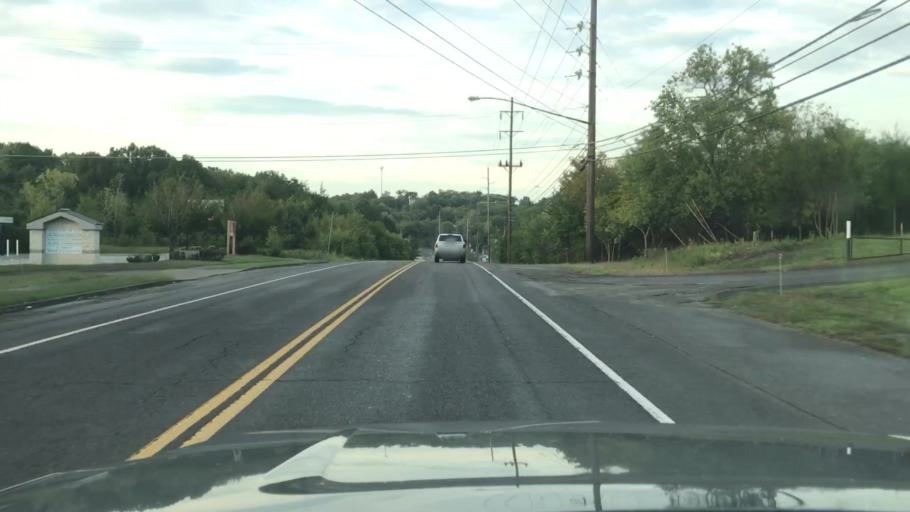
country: US
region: Tennessee
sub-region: Davidson County
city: Nashville
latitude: 36.2153
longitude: -86.8378
